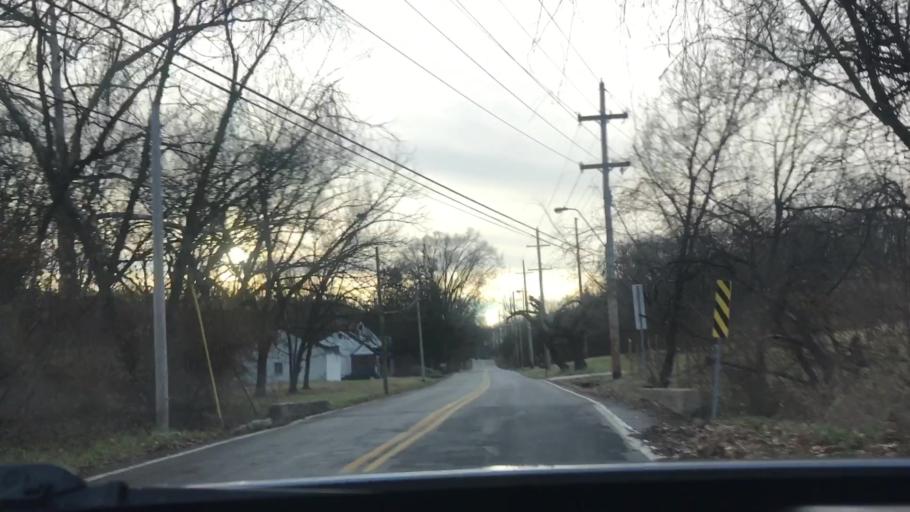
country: US
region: Missouri
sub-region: Platte County
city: Riverside
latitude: 39.2193
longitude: -94.6240
